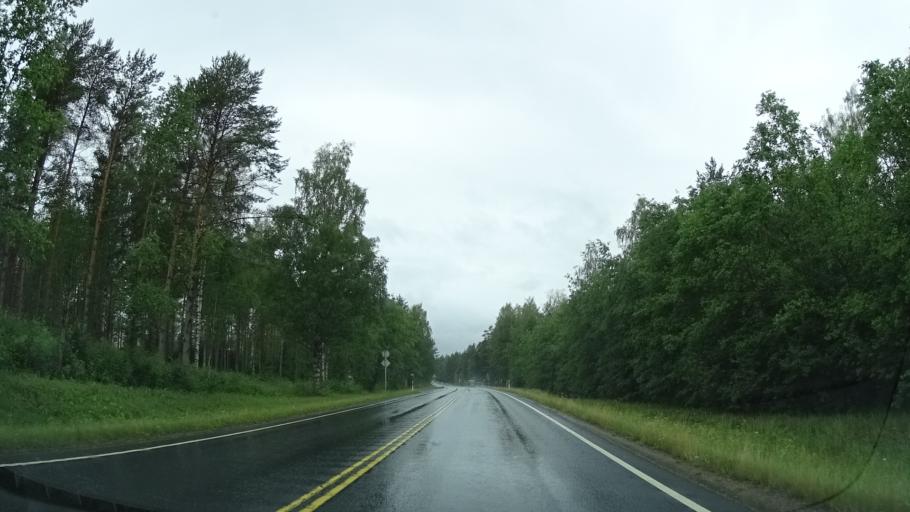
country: FI
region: Haeme
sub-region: Forssa
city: Humppila
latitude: 60.9633
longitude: 23.3161
